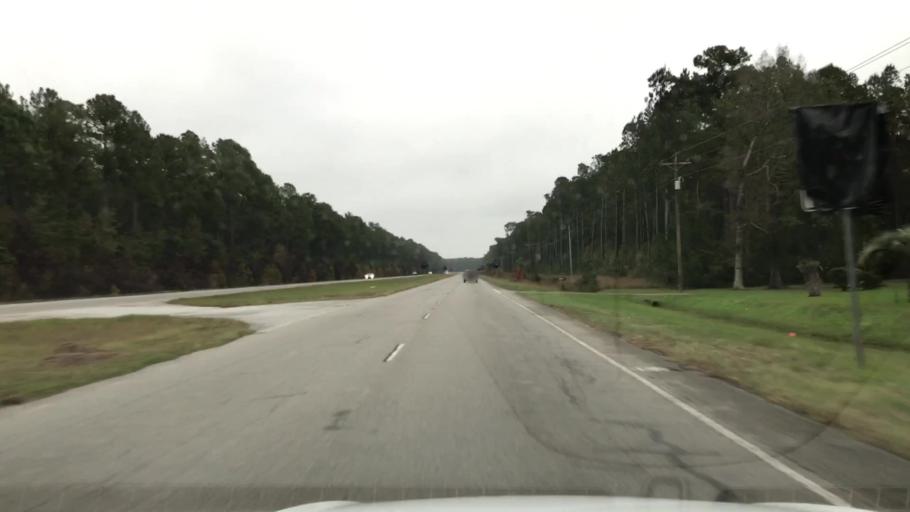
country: US
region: South Carolina
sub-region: Charleston County
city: Awendaw
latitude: 33.0453
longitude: -79.5799
